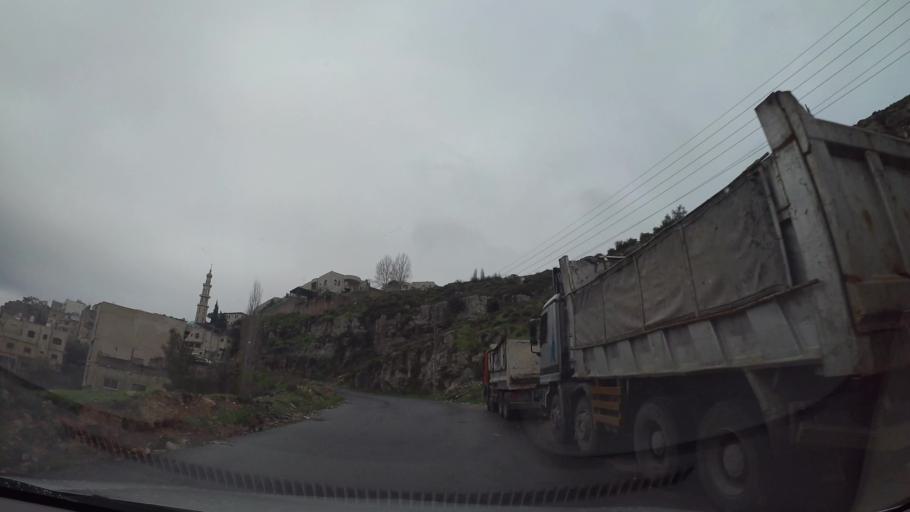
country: JO
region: Amman
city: Al Jubayhah
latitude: 32.0323
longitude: 35.8314
